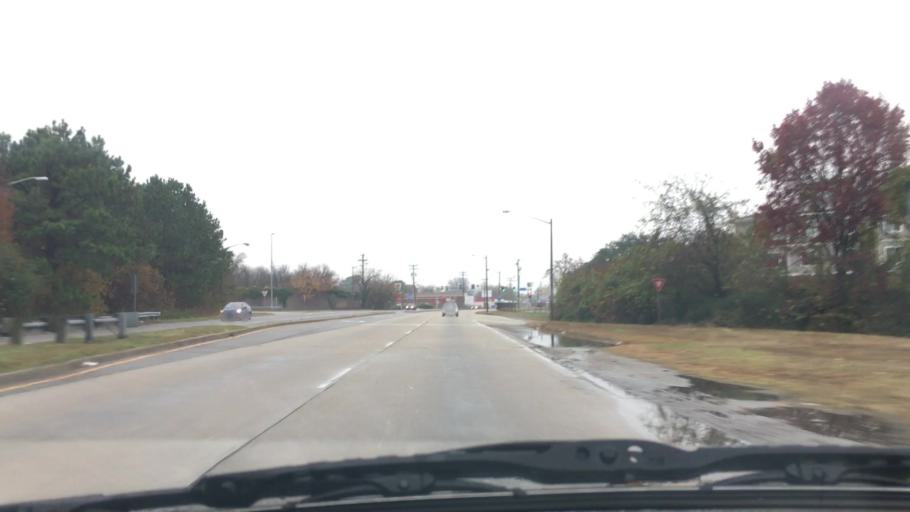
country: US
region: Virginia
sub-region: City of Norfolk
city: Norfolk
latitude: 36.9073
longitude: -76.2564
